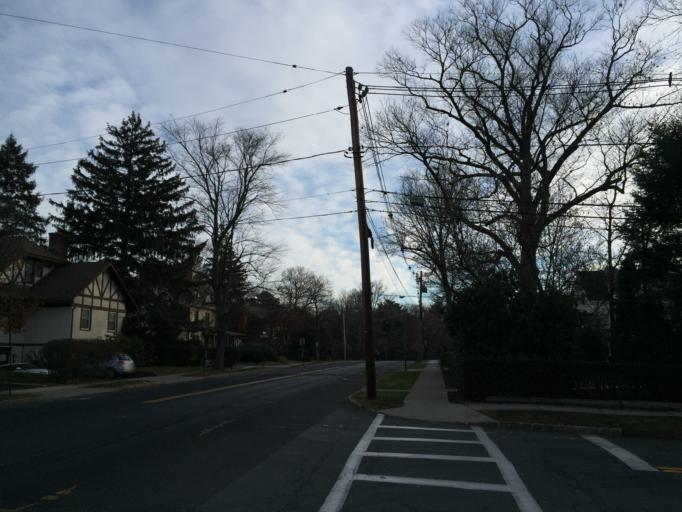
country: US
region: New Jersey
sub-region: Union County
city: Summit
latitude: 40.7184
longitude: -74.3537
